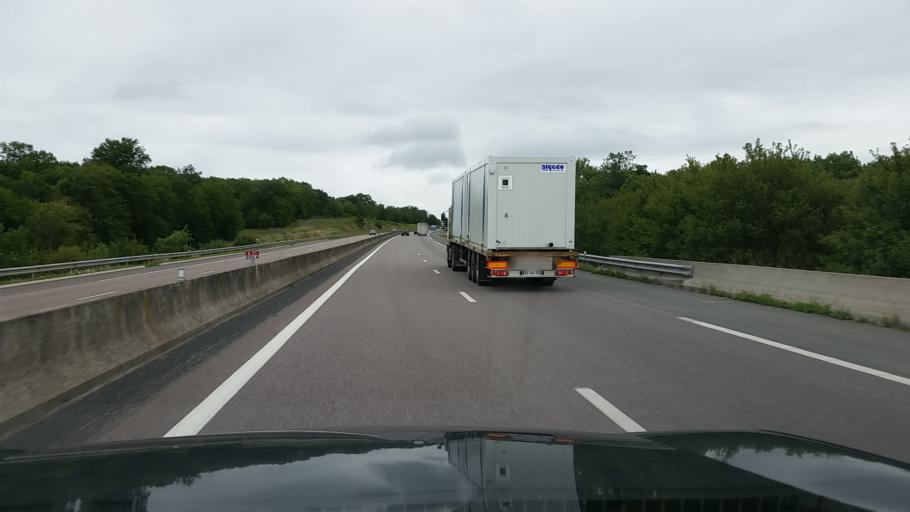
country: FR
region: Lorraine
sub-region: Departement de Meurthe-et-Moselle
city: Colombey-les-Belles
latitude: 48.4623
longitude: 5.8713
